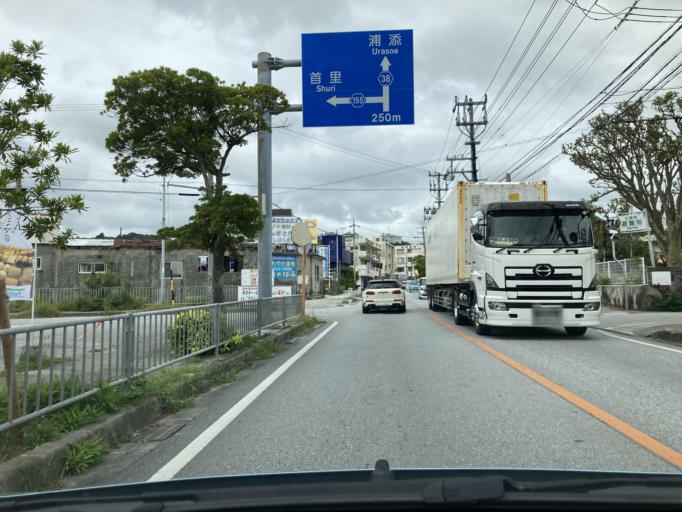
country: JP
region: Okinawa
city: Ginowan
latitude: 26.2273
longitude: 127.7553
